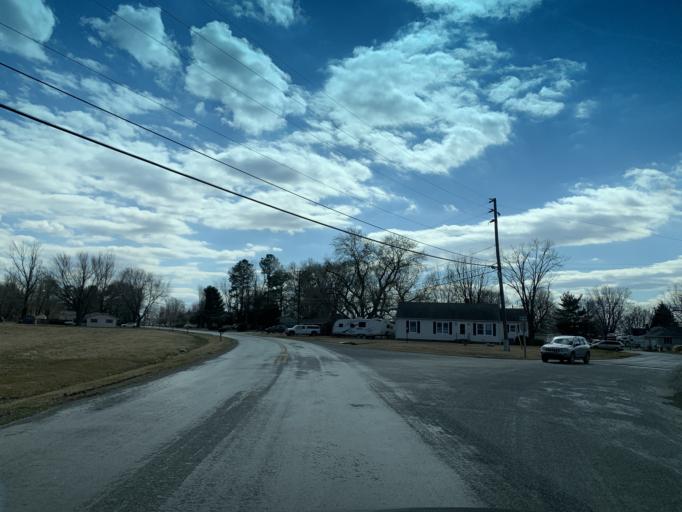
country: US
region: Maryland
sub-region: Queen Anne's County
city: Chester
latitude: 38.9419
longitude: -76.2661
